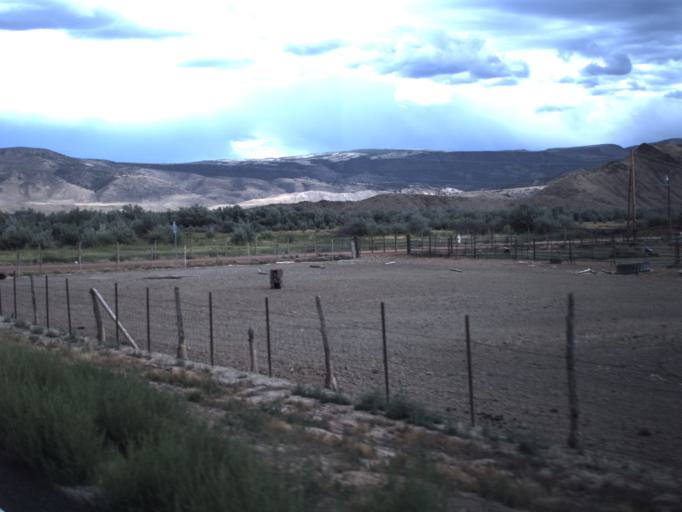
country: US
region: Utah
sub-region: Sevier County
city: Richfield
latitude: 38.7741
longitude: -112.0253
